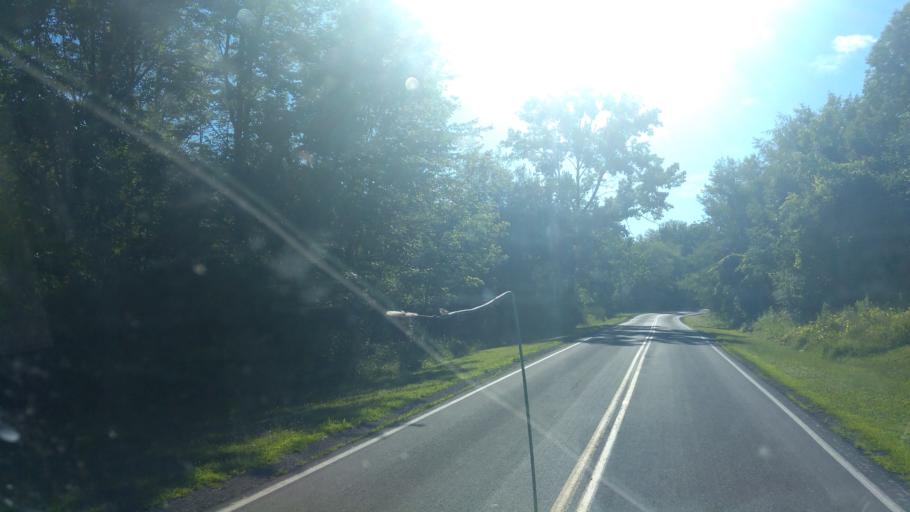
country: US
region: New York
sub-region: Wayne County
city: Lyons
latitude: 42.9964
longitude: -76.9399
